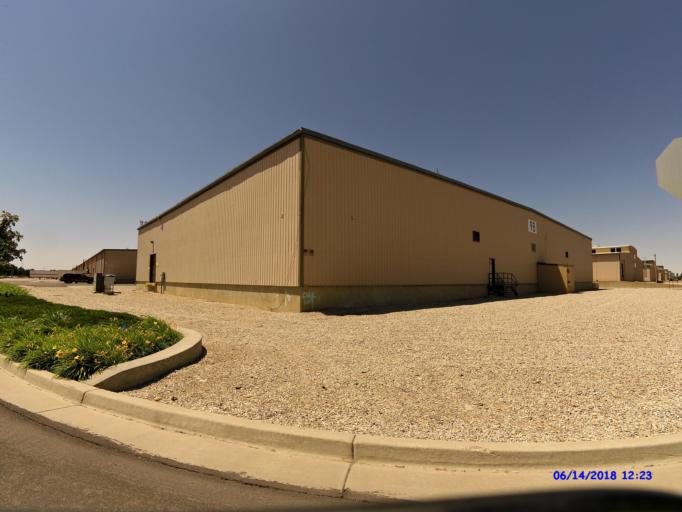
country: US
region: Utah
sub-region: Weber County
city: Harrisville
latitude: 41.2632
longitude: -111.9987
